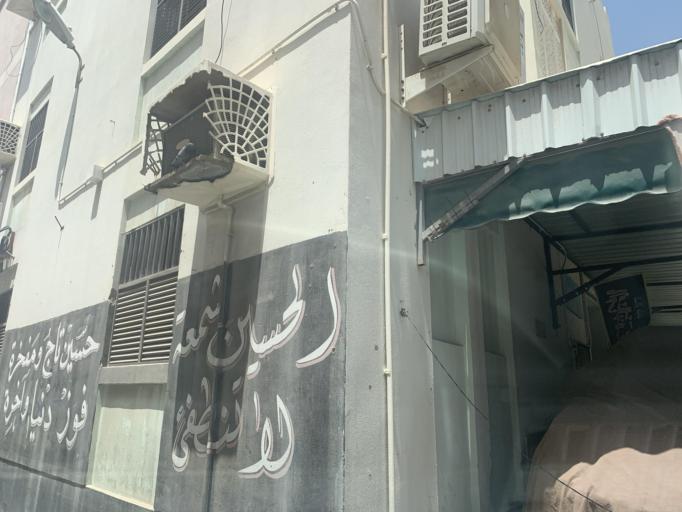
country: BH
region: Manama
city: Jidd Hafs
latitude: 26.2179
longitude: 50.5373
